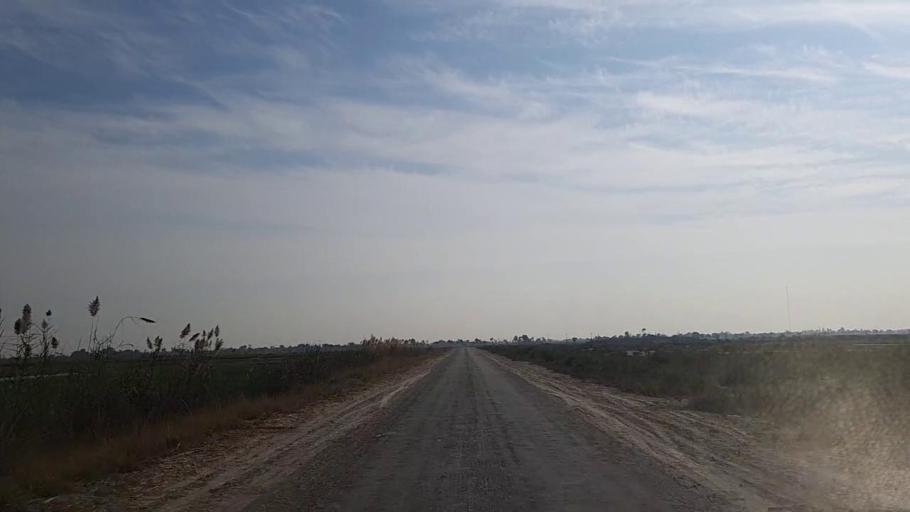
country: PK
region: Sindh
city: Daur
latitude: 26.4807
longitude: 68.4128
